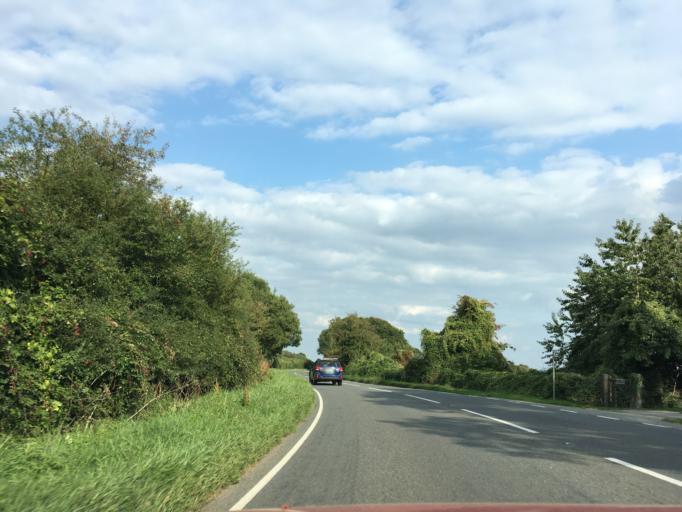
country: GB
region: England
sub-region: Gloucestershire
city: Nailsworth
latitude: 51.6470
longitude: -2.2197
